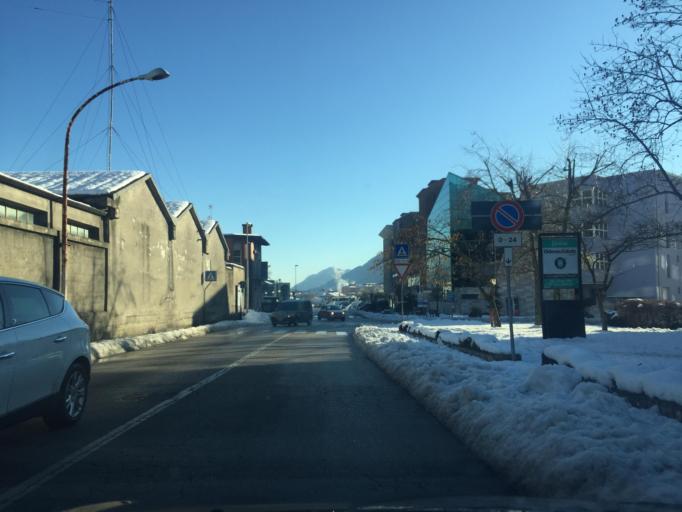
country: IT
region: Friuli Venezia Giulia
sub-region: Provincia di Udine
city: Tolmezzo
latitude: 46.4064
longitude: 13.0102
